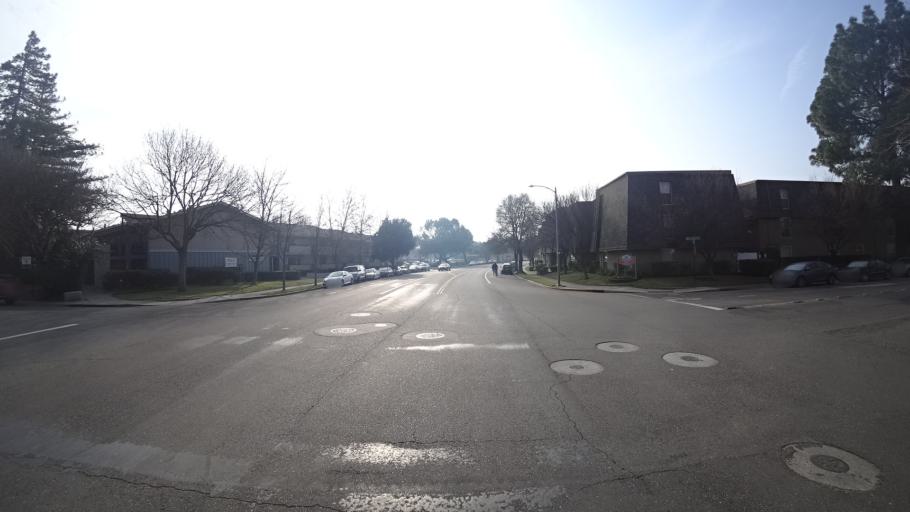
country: US
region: California
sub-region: Yolo County
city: Davis
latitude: 38.5486
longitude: -121.7624
